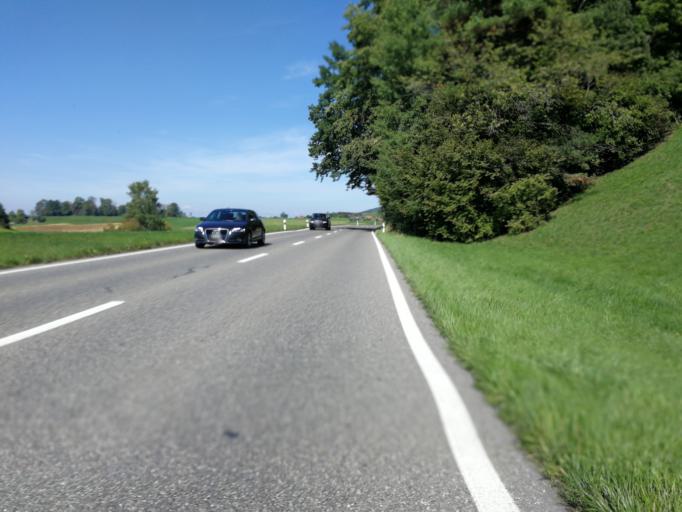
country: CH
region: Zurich
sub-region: Bezirk Hinwil
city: Wetzikon / Kempten
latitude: 47.3147
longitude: 8.8273
